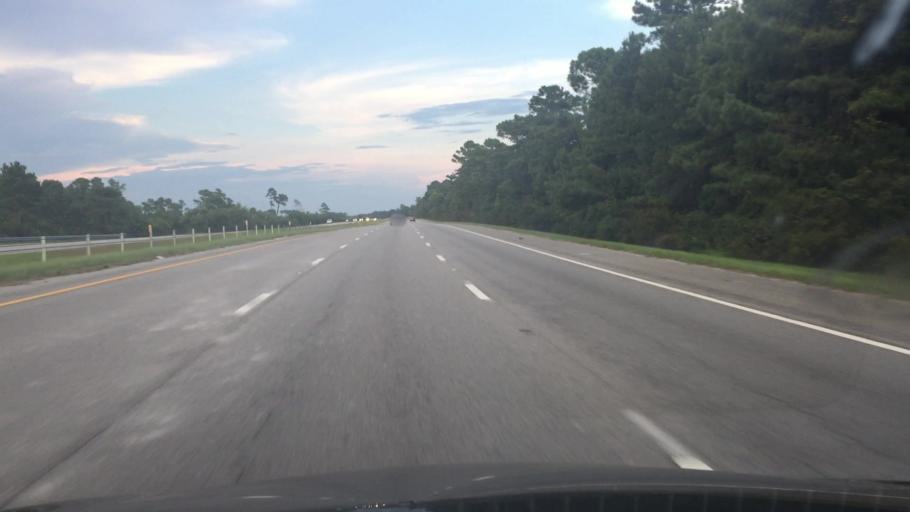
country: US
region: South Carolina
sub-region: Horry County
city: Myrtle Beach
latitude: 33.7658
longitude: -78.8327
